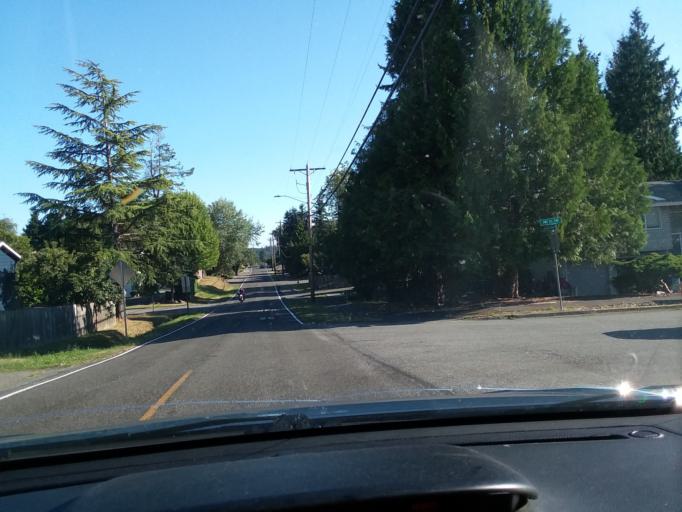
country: US
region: Washington
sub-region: Snohomish County
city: Alderwood Manor
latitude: 47.8258
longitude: -122.2871
